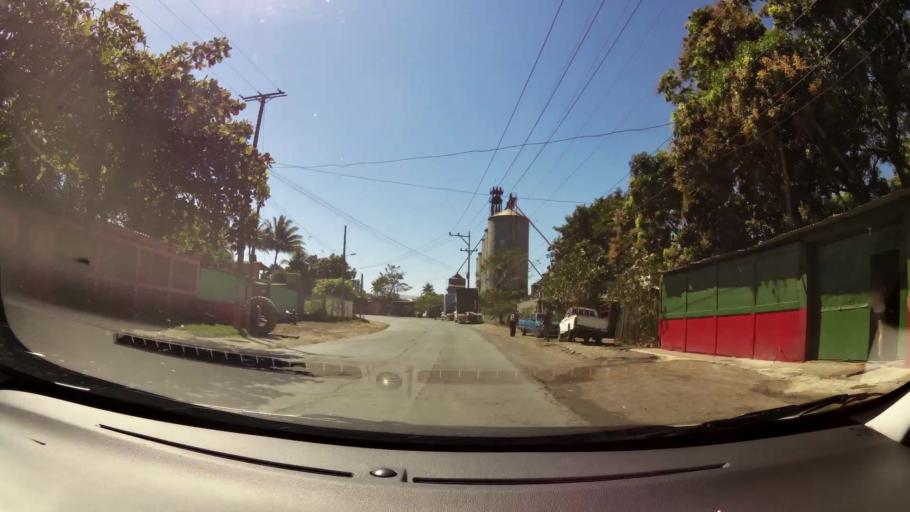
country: SV
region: La Libertad
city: Ciudad Arce
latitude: 13.7824
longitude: -89.3727
